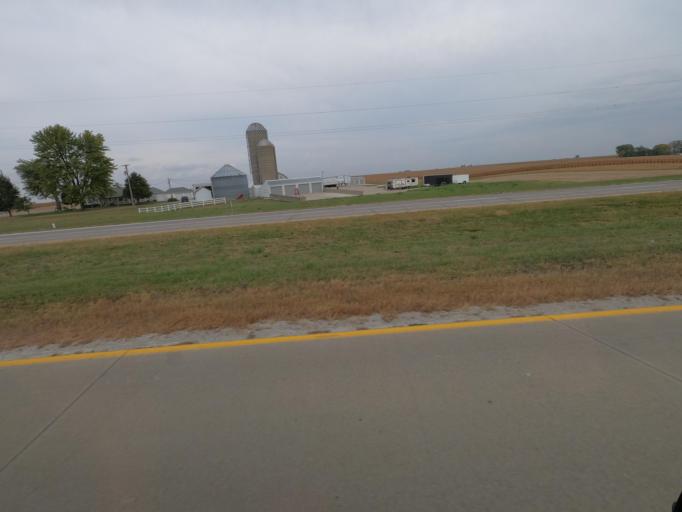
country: US
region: Iowa
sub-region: Marion County
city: Pella
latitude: 41.4430
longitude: -93.0138
